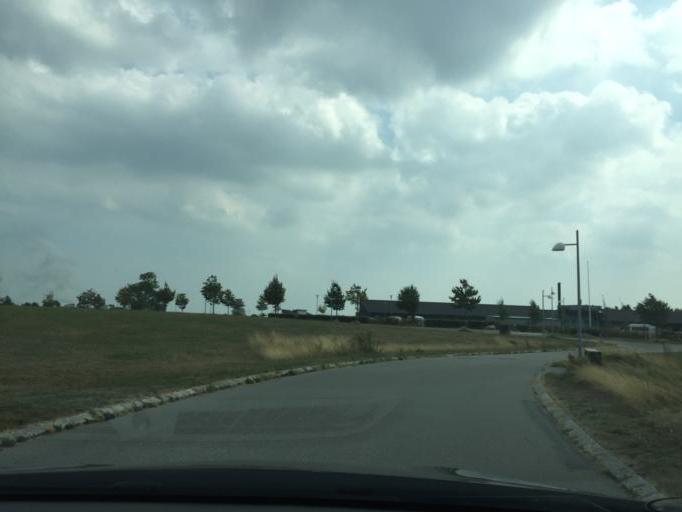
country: DK
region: South Denmark
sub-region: Nyborg Kommune
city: Nyborg
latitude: 55.3159
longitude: 10.7615
